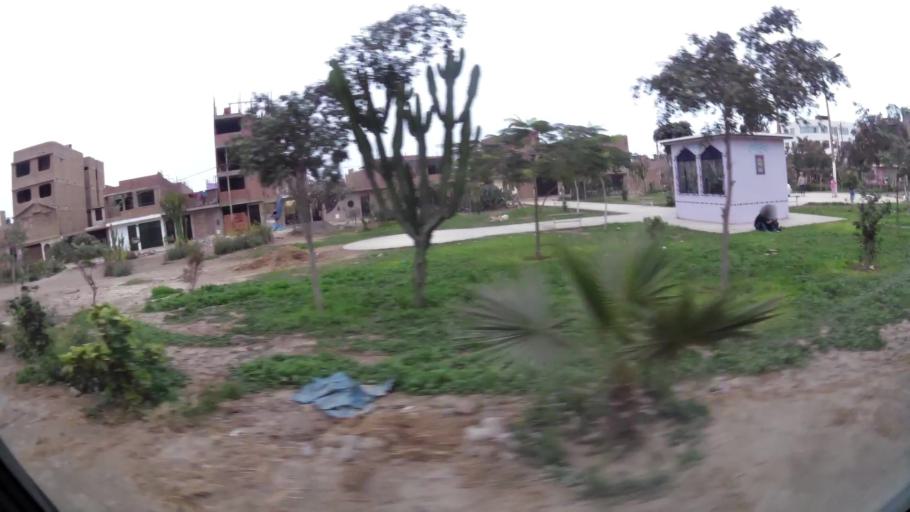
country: PE
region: Lima
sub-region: Lima
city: Independencia
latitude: -11.9798
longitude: -77.1003
